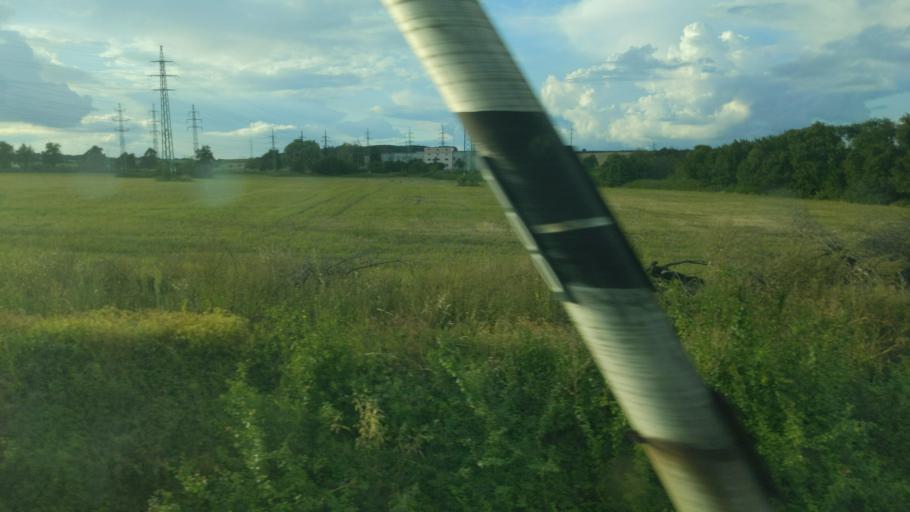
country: CZ
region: Central Bohemia
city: Cesky Brod
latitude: 50.0828
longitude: 14.8867
